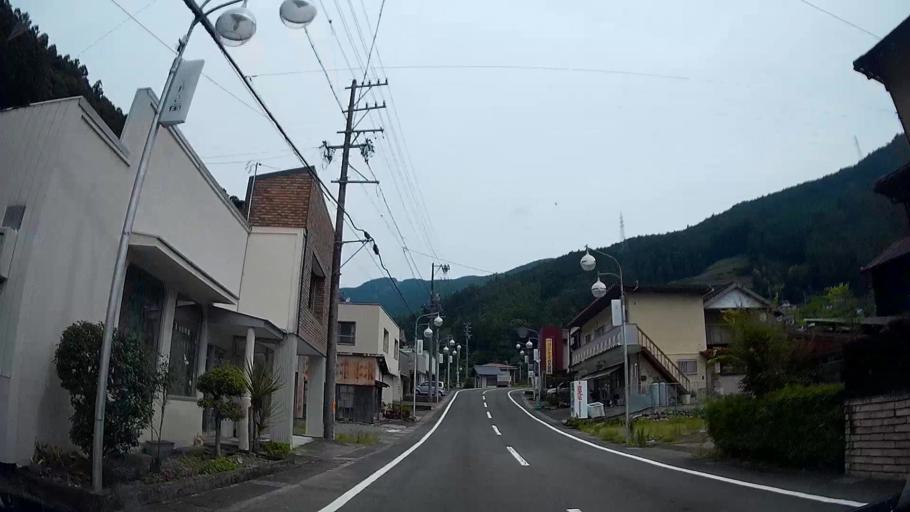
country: JP
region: Shizuoka
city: Hamakita
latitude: 34.9436
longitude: 137.8160
